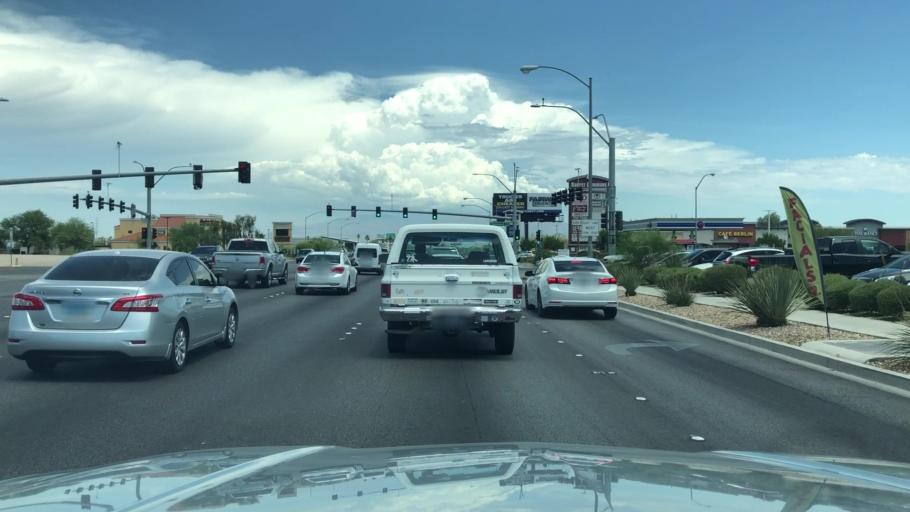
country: US
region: Nevada
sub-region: Clark County
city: Spring Valley
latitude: 36.0711
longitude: -115.2078
